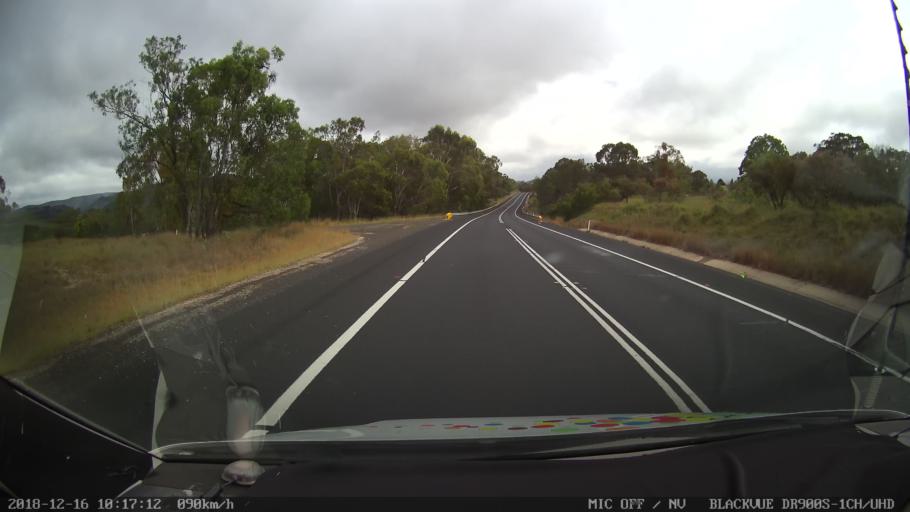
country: AU
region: New South Wales
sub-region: Tenterfield Municipality
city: Carrolls Creek
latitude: -29.2586
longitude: 151.9895
